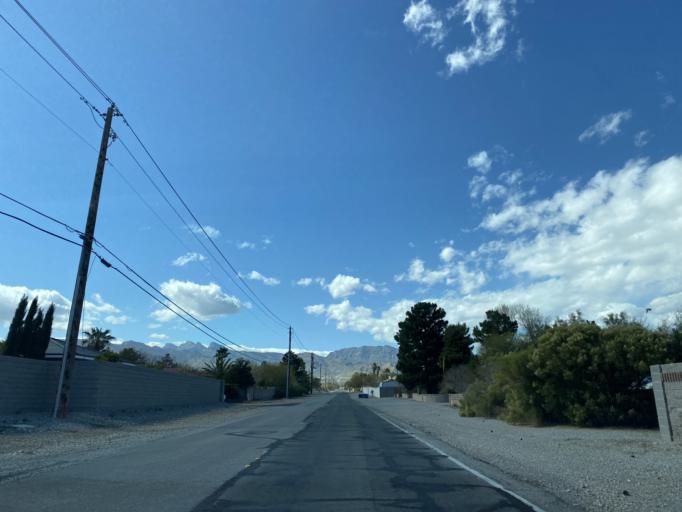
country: US
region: Nevada
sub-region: Clark County
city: Summerlin South
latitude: 36.2555
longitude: -115.2816
